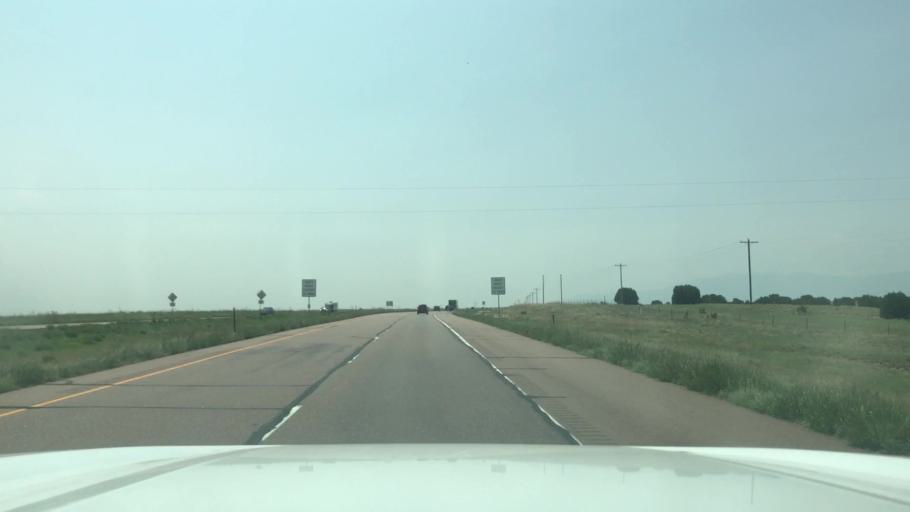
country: US
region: Colorado
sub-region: Pueblo County
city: Pueblo
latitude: 38.1127
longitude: -104.6750
